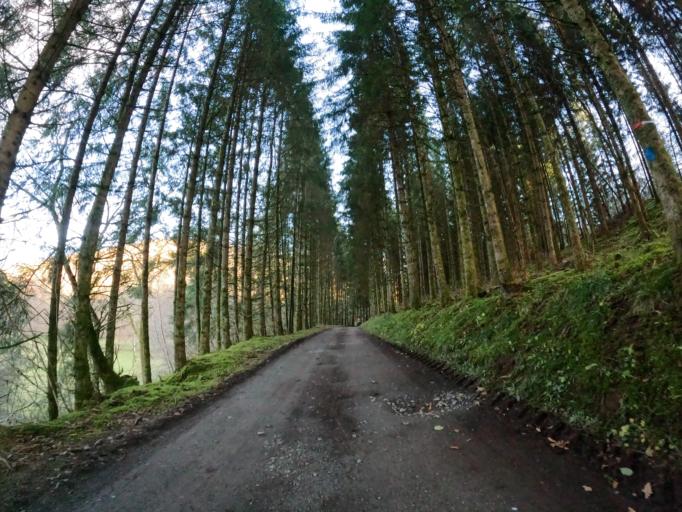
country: LU
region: Diekirch
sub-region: Canton de Wiltz
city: Bavigne
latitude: 49.9548
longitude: 5.8396
